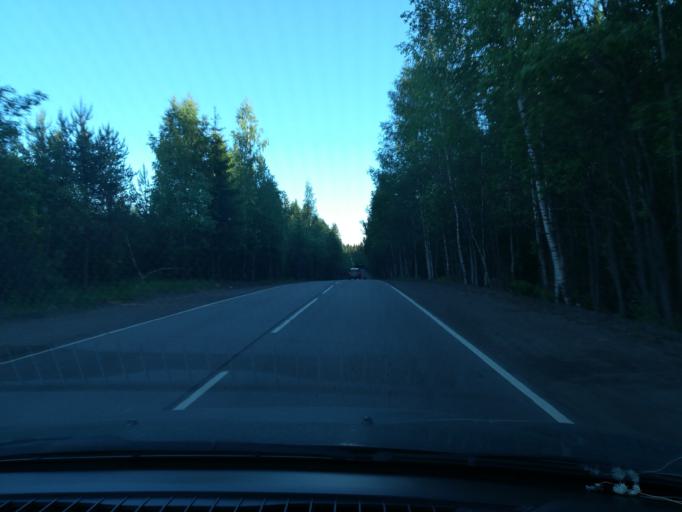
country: RU
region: Leningrad
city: Lesogorskiy
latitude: 60.9903
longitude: 28.9098
